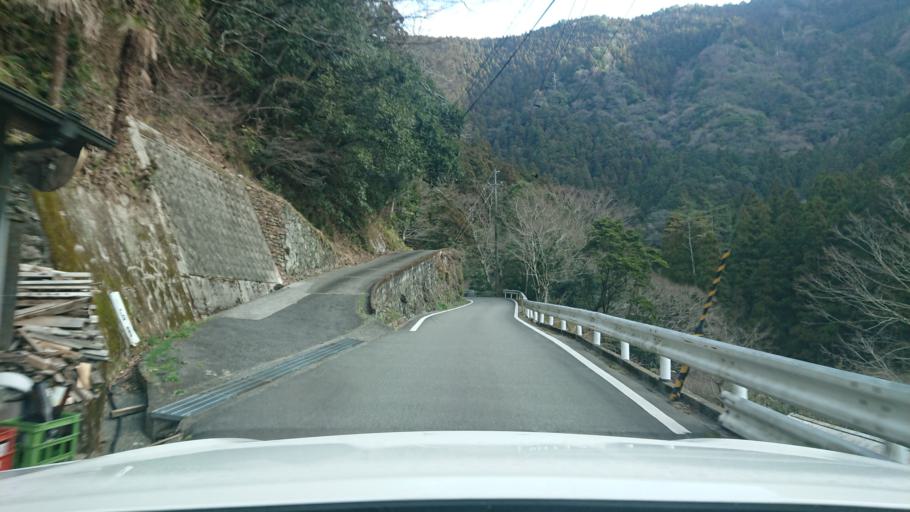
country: JP
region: Tokushima
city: Kamojimacho-jogejima
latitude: 33.9043
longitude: 134.3945
